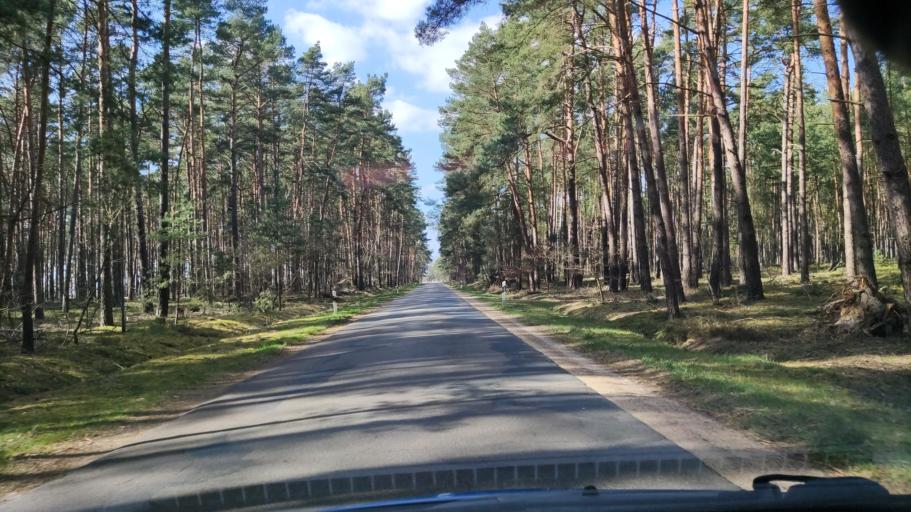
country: DE
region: Lower Saxony
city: Trebel
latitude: 53.0015
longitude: 11.2868
